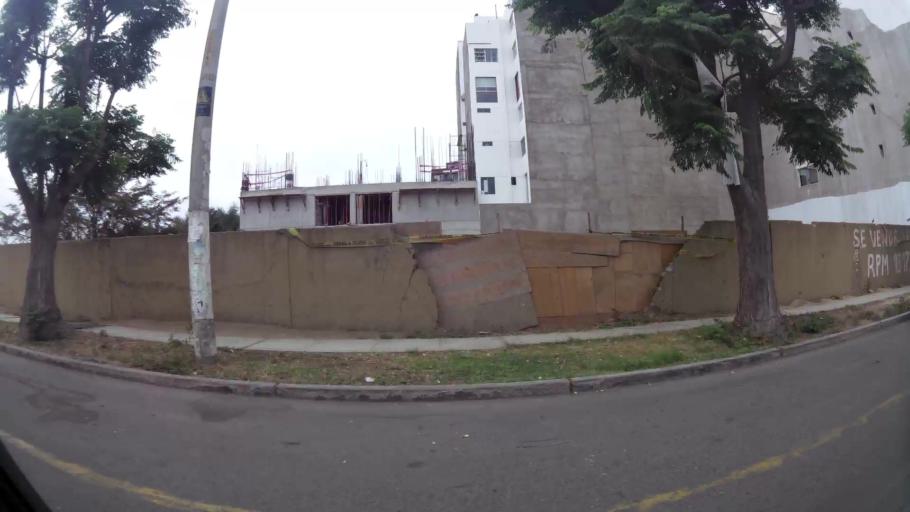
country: PE
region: La Libertad
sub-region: Provincia de Trujillo
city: Buenos Aires
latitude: -8.1349
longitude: -79.0387
